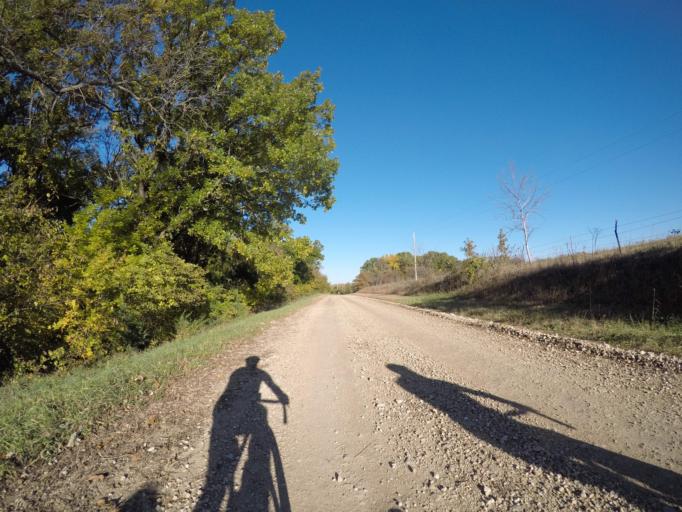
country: US
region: Kansas
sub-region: Wabaunsee County
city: Alma
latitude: 38.9305
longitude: -96.4741
